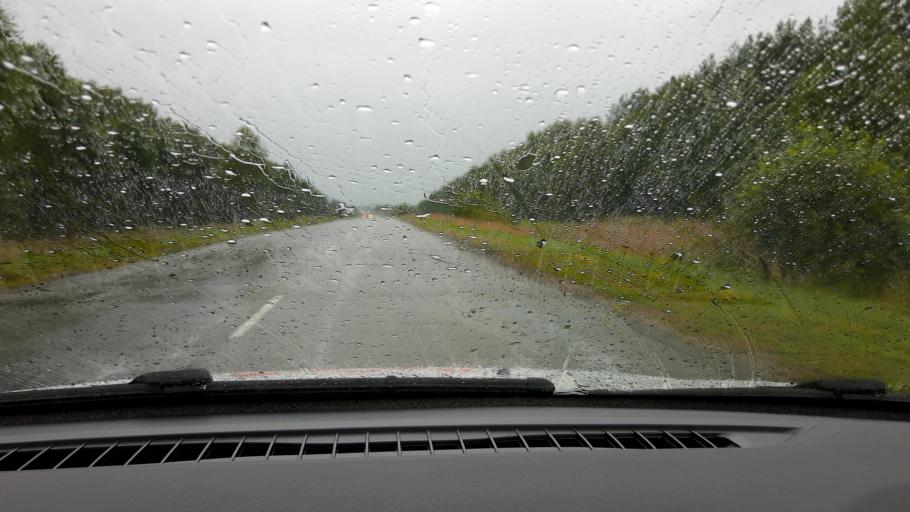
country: RU
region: Nizjnij Novgorod
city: Satis
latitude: 54.8901
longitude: 43.0821
